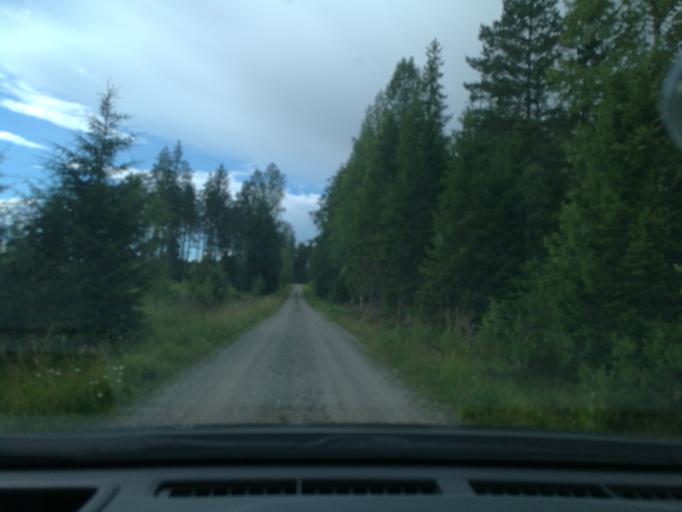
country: SE
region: Vaestmanland
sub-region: Surahammars Kommun
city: Ramnas
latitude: 59.8192
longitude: 16.2698
